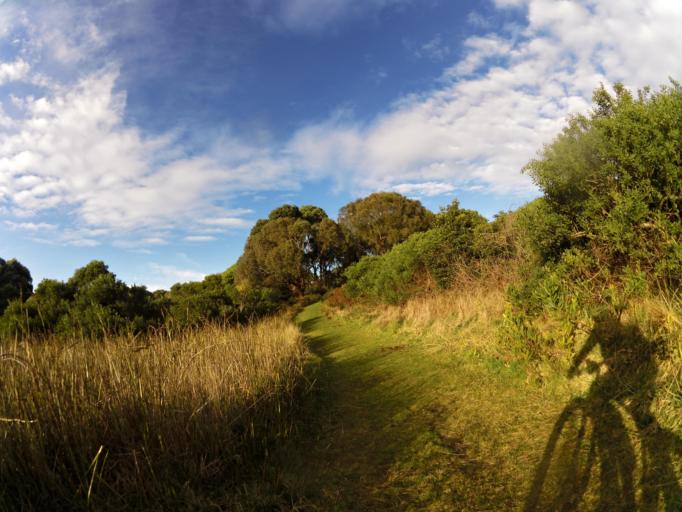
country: AU
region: Victoria
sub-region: Bass Coast
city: North Wonthaggi
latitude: -38.6035
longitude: 145.5623
